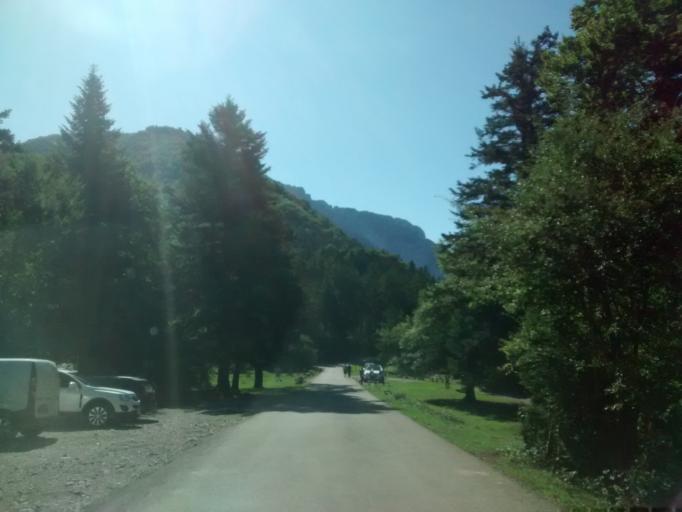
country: ES
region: Aragon
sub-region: Provincia de Huesca
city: Aragues del Puerto
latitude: 42.8336
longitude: -0.7111
